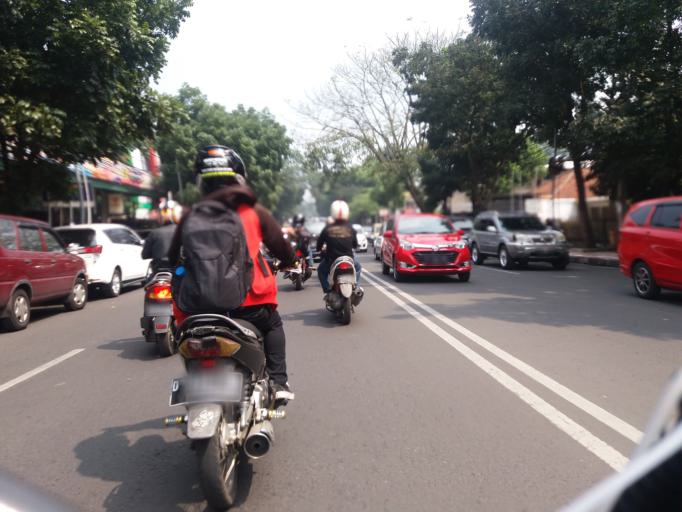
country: ID
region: West Java
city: Bandung
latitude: -6.9066
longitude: 107.5957
